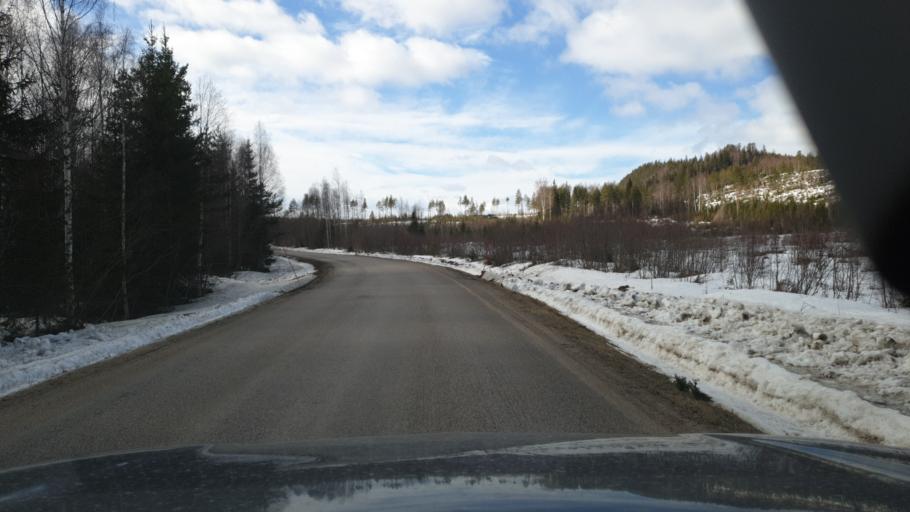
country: SE
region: Gaevleborg
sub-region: Ljusdals Kommun
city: Farila
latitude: 61.8452
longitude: 15.9411
